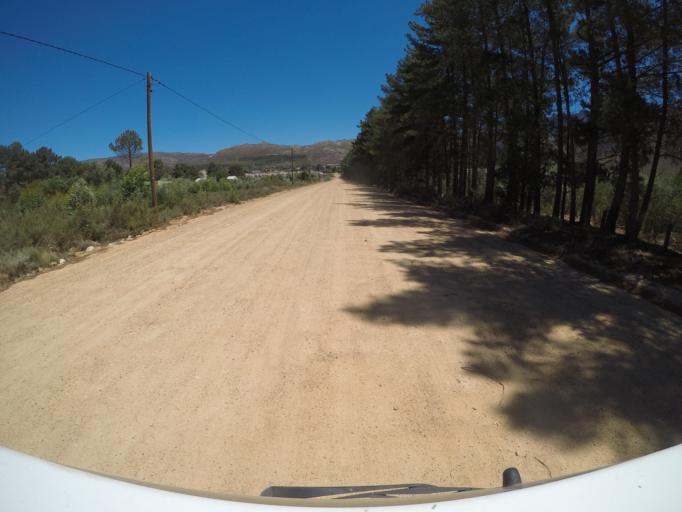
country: ZA
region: Western Cape
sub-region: Overberg District Municipality
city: Grabouw
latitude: -34.2232
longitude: 19.1996
